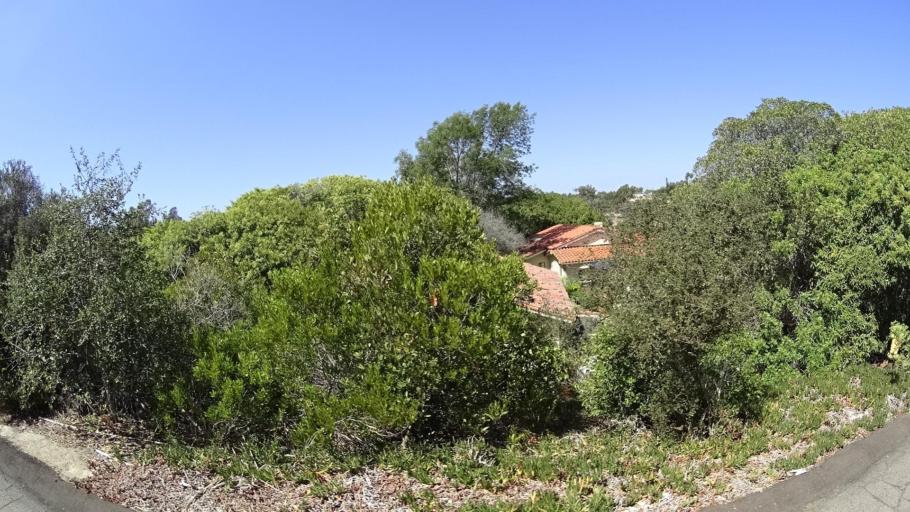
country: US
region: California
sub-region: San Diego County
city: Rancho Santa Fe
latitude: 33.0213
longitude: -117.2225
